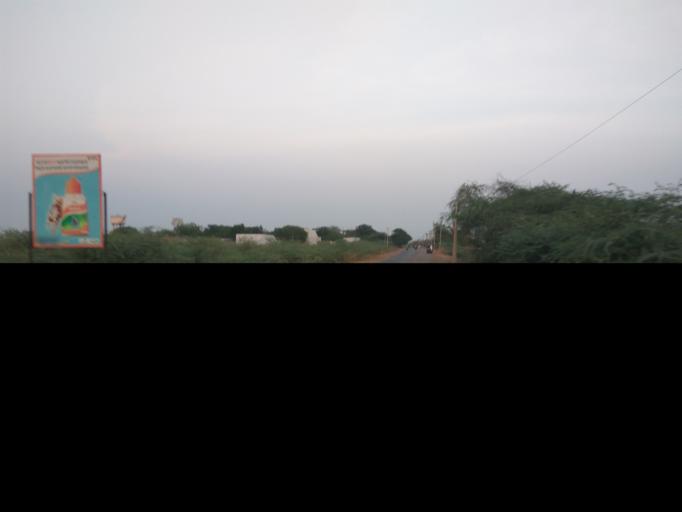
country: IN
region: Andhra Pradesh
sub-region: Prakasam
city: Markapur
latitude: 15.7406
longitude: 79.2509
